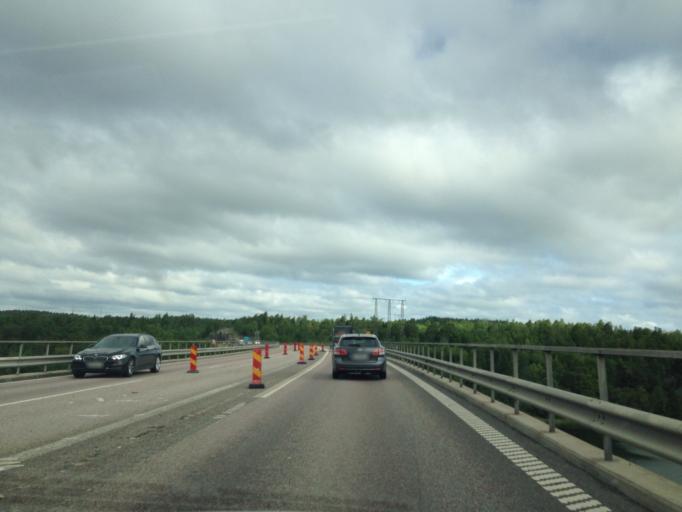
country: SE
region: Stockholm
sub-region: Varmdo Kommun
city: Gustavsberg
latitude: 59.3193
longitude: 18.3488
